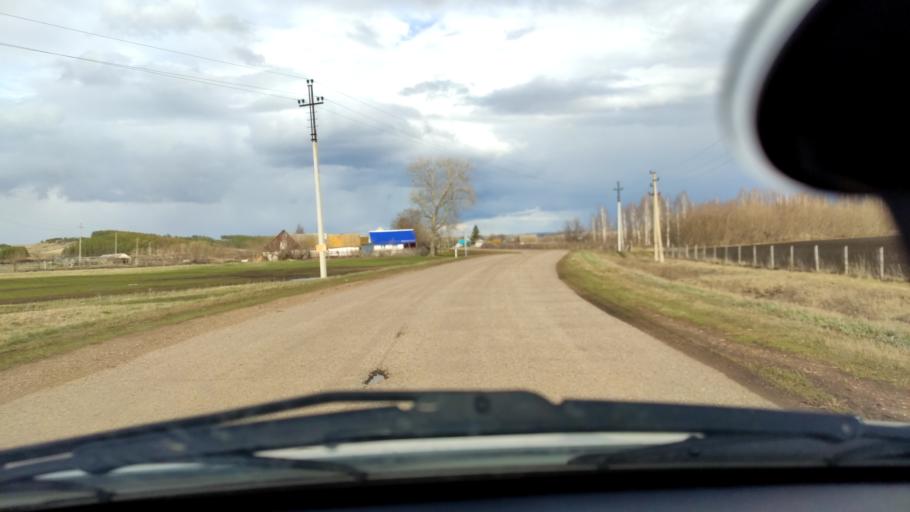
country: RU
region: Bashkortostan
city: Buzdyak
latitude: 54.7673
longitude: 54.5963
